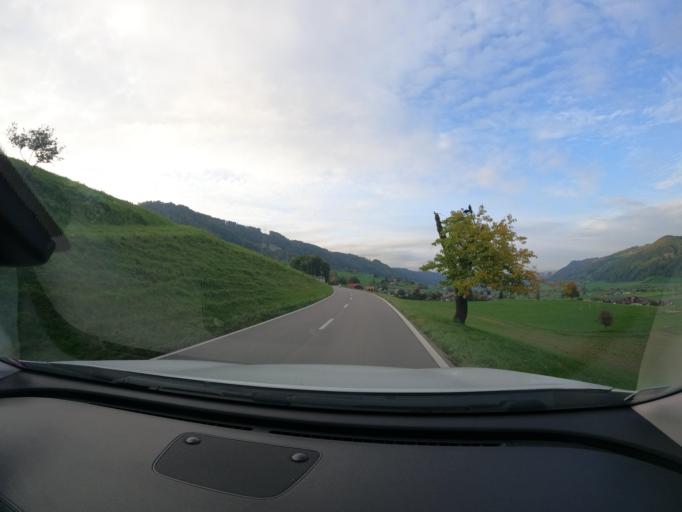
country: CH
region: Bern
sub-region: Bern-Mittelland District
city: Hermiswil
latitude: 46.8334
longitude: 7.4968
